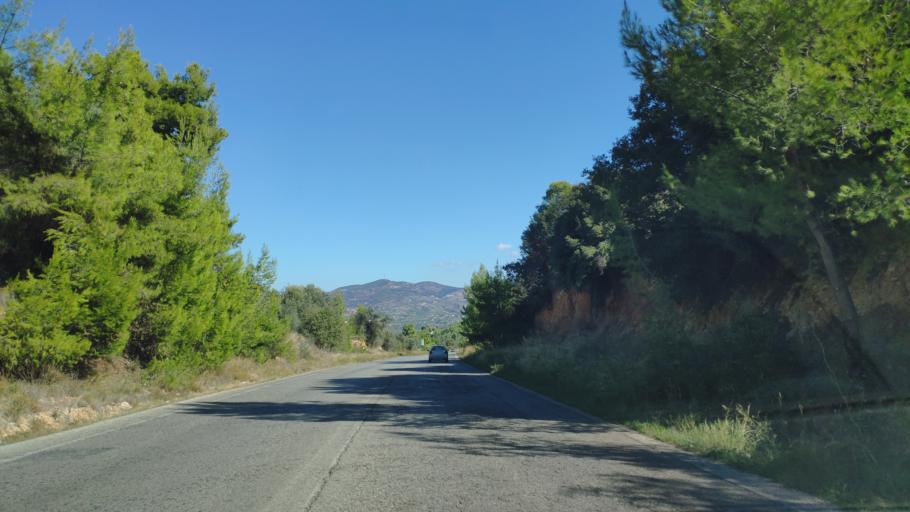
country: GR
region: Peloponnese
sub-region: Nomos Korinthias
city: Khiliomodhi
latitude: 37.8199
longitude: 22.8766
